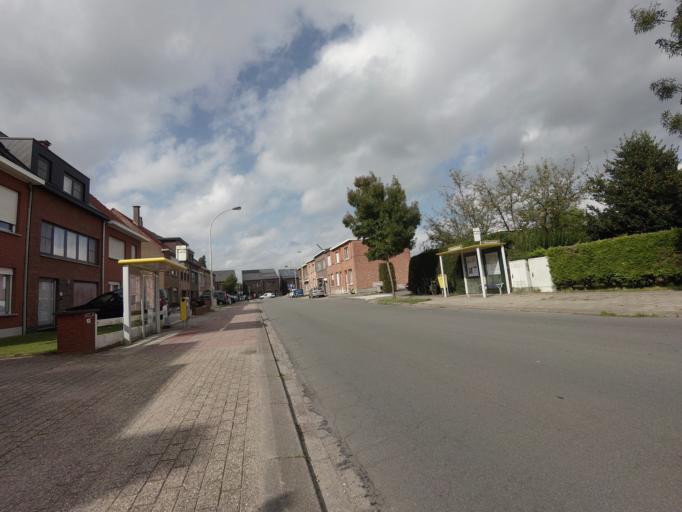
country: BE
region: Flanders
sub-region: Provincie Antwerpen
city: Boom
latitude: 51.1105
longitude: 4.3827
